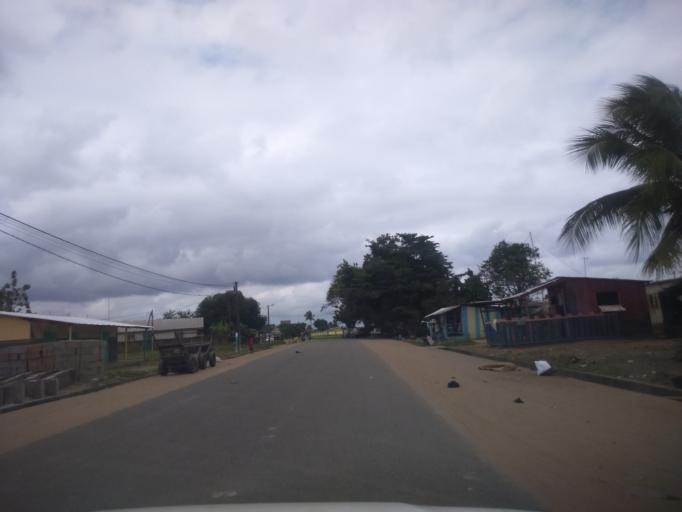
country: CI
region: Sud-Comoe
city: Adiake
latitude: 5.2883
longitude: -3.3033
